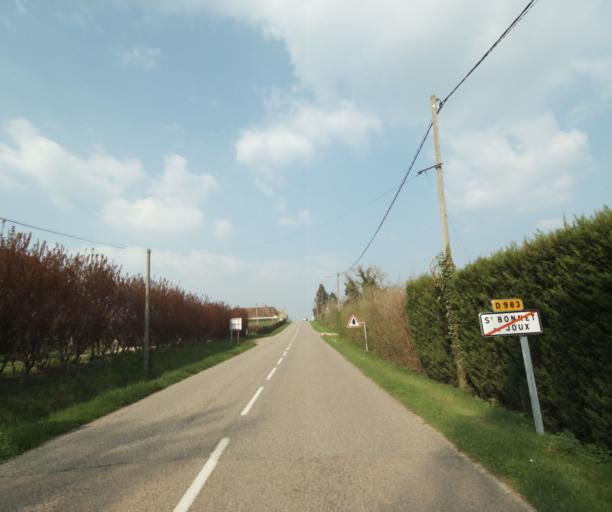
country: FR
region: Bourgogne
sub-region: Departement de Saone-et-Loire
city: Charolles
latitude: 46.4870
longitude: 4.4435
